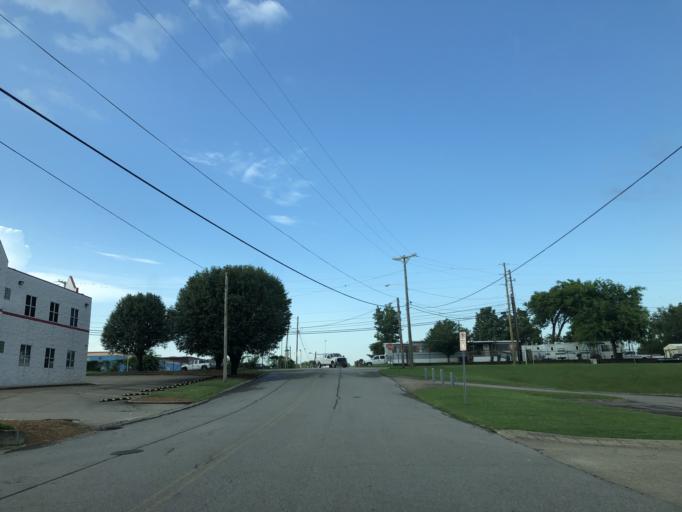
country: US
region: Tennessee
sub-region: Davidson County
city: Nashville
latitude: 36.1364
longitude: -86.7325
